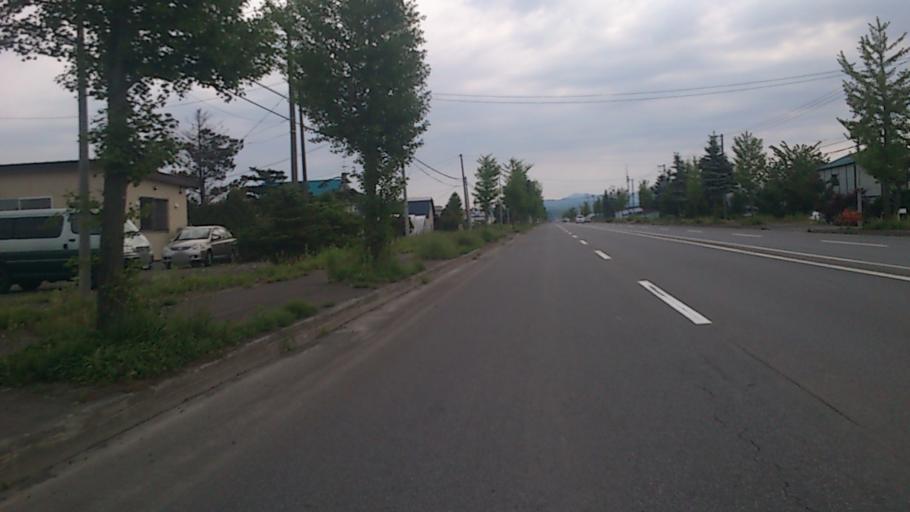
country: JP
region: Hokkaido
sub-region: Asahikawa-shi
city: Asahikawa
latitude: 43.8390
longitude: 142.4794
